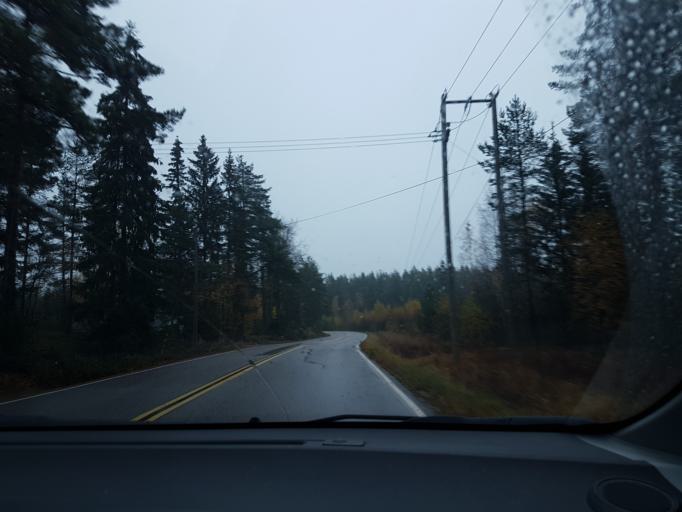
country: FI
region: Uusimaa
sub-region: Helsinki
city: Jaervenpaeae
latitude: 60.5844
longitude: 25.1757
